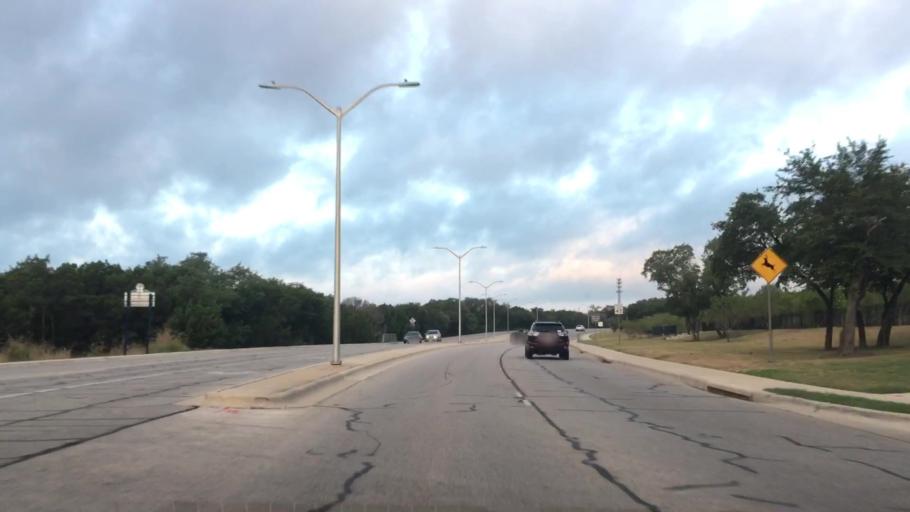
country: US
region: Texas
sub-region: Williamson County
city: Brushy Creek
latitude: 30.5073
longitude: -97.7772
